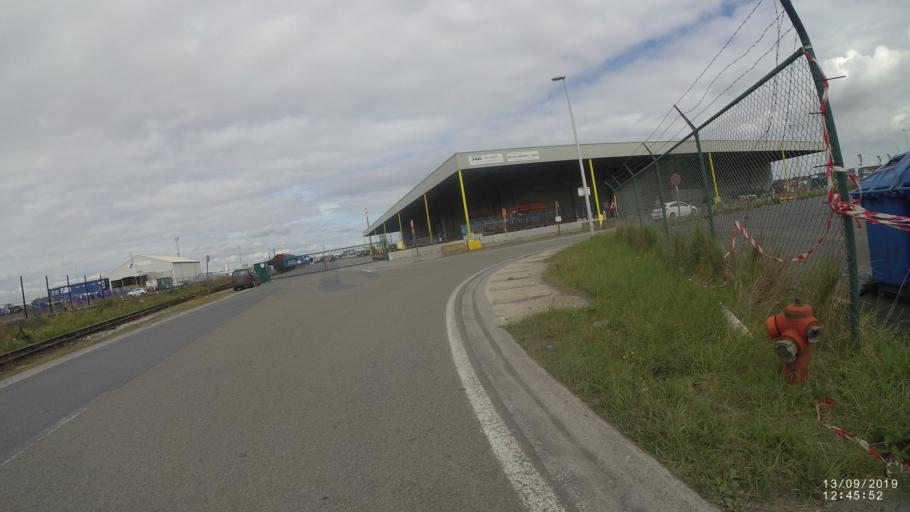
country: BE
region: Flanders
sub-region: Provincie Oost-Vlaanderen
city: Evergem
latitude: 51.1136
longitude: 3.7617
